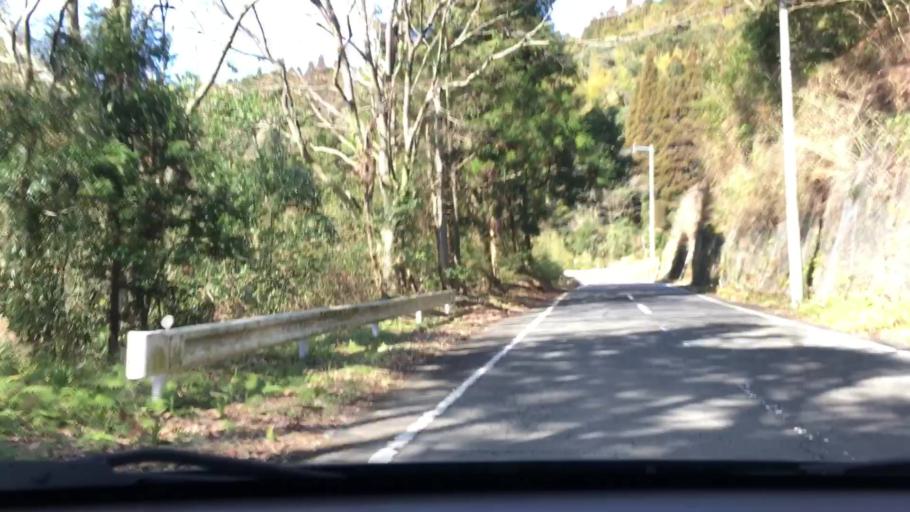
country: JP
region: Kagoshima
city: Ijuin
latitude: 31.7126
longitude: 130.4172
